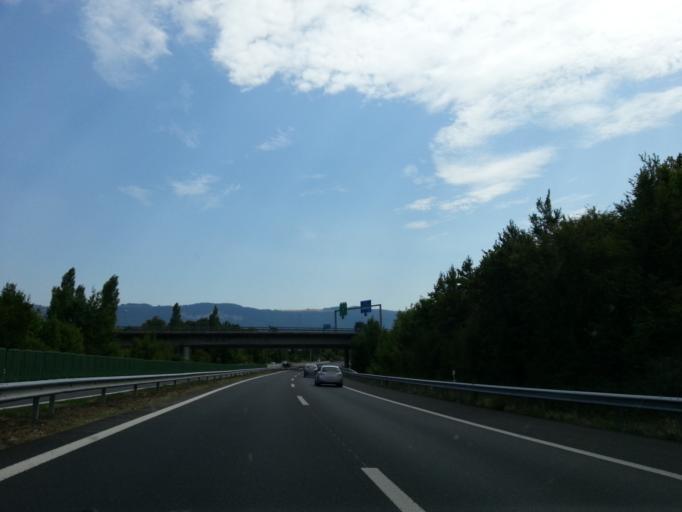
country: CH
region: Geneva
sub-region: Geneva
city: Confignon
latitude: 46.1645
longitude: 6.0997
